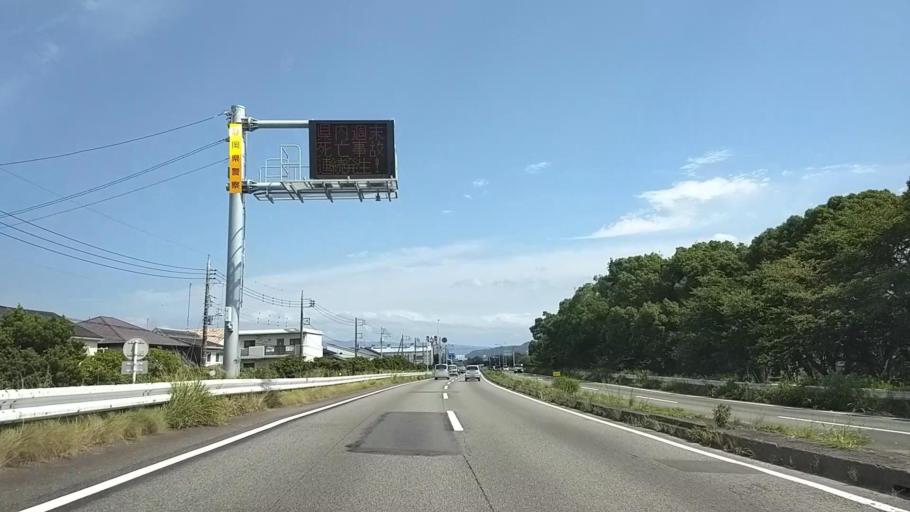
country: JP
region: Shizuoka
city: Numazu
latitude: 35.1227
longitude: 138.8184
